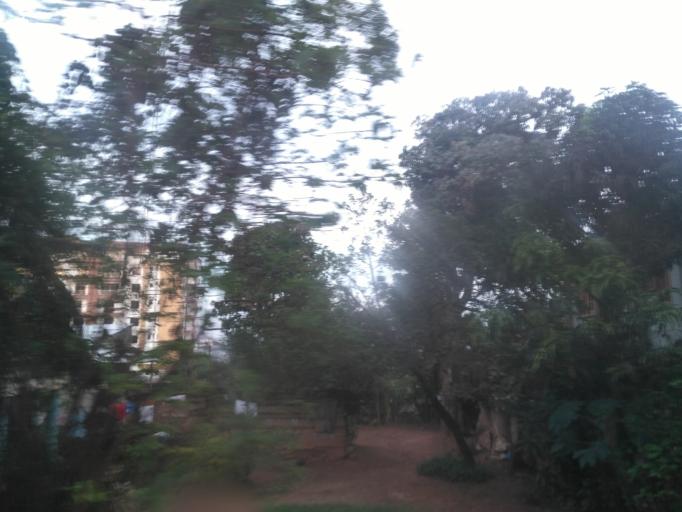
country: UG
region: Central Region
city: Kampala Central Division
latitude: 0.3417
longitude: 32.5827
